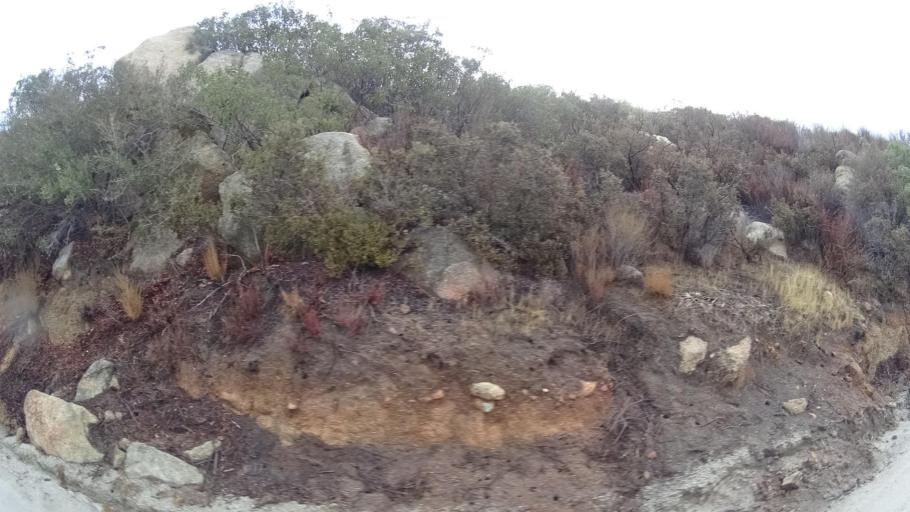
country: MX
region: Baja California
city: Tecate
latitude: 32.6006
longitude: -116.6394
